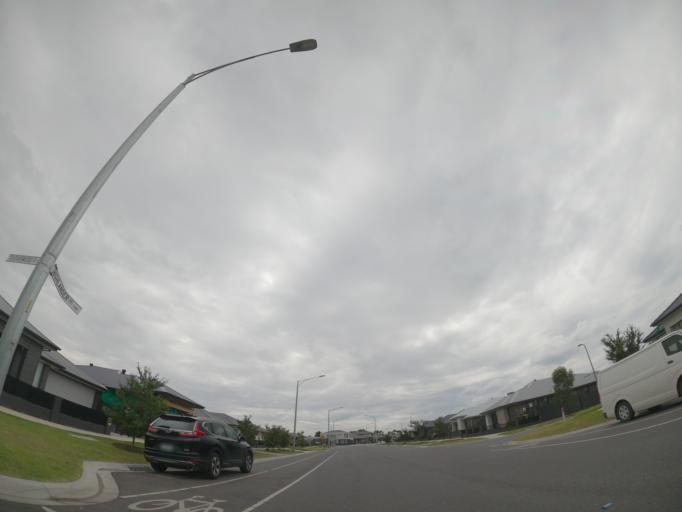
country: AU
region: Victoria
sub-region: Hume
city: Craigieburn
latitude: -37.5678
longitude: 144.8966
